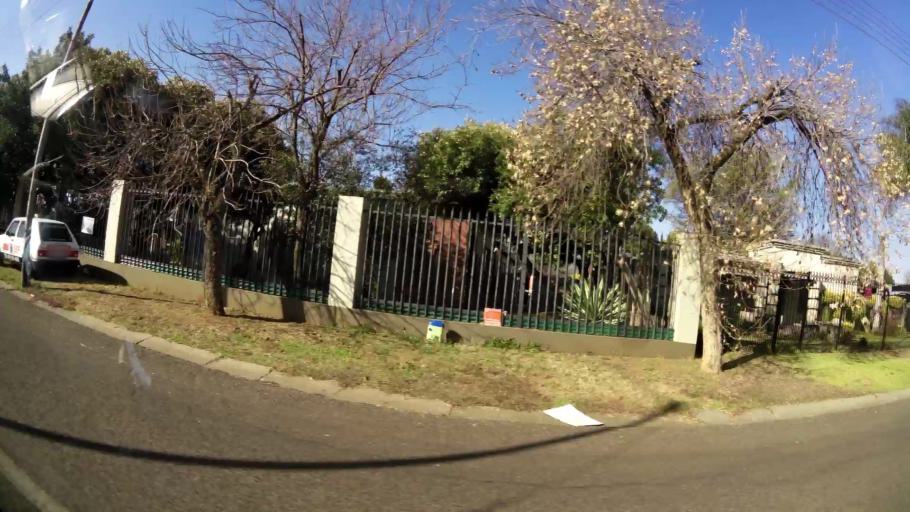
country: ZA
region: Gauteng
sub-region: City of Tshwane Metropolitan Municipality
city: Pretoria
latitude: -25.7279
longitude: 28.2628
